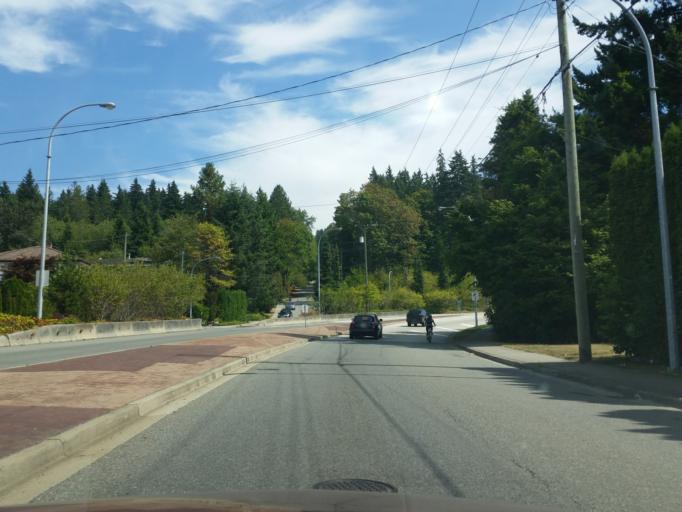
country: CA
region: British Columbia
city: Burnaby
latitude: 49.2804
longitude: -122.9519
